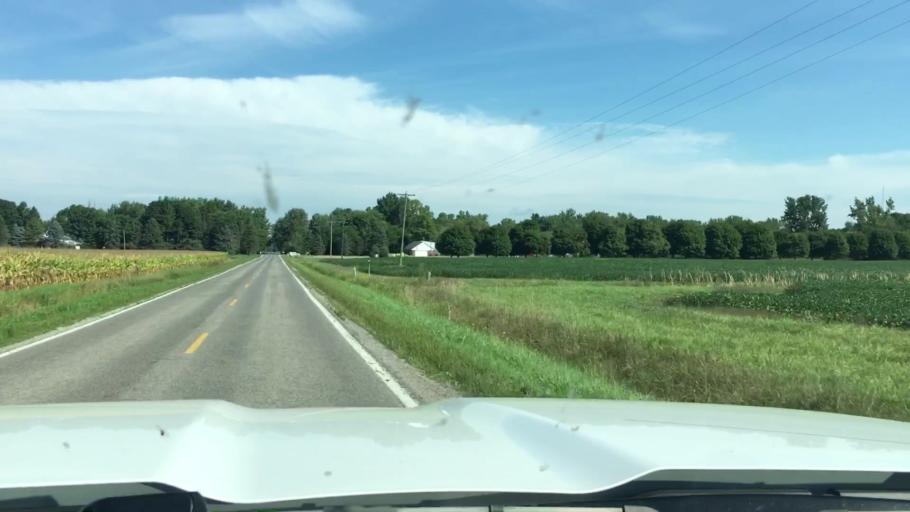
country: US
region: Michigan
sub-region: Saginaw County
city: Hemlock
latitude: 43.4683
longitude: -84.2303
